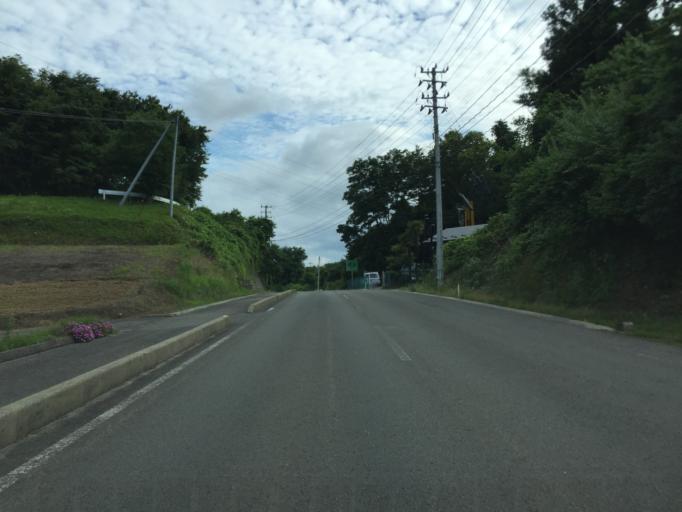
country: JP
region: Fukushima
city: Fukushima-shi
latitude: 37.6900
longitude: 140.5018
